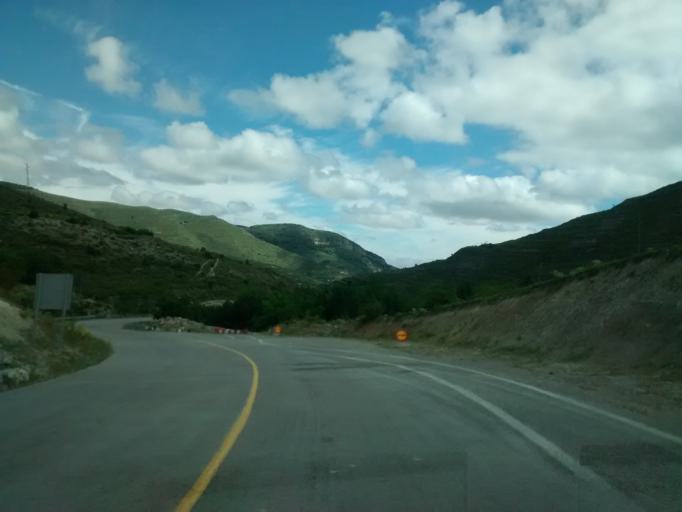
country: ES
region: La Rioja
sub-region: Provincia de La Rioja
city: Terroba
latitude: 42.2688
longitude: -2.4329
